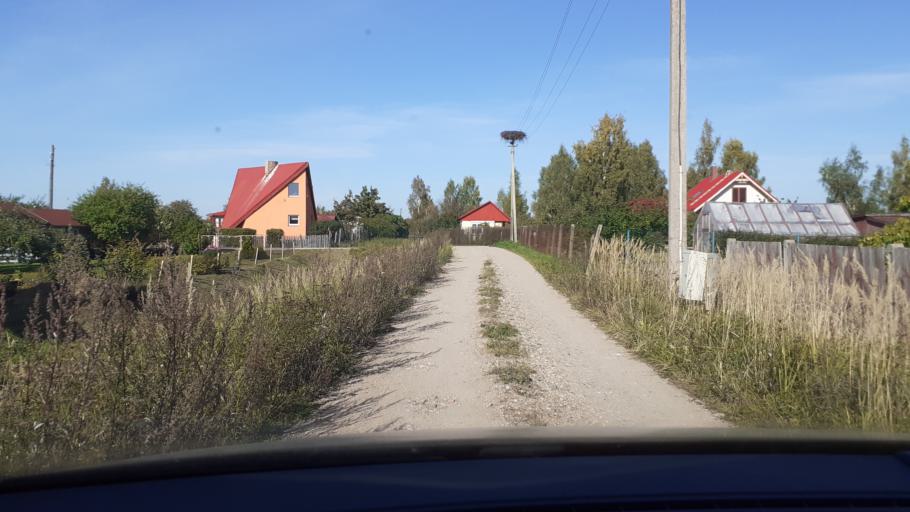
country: LV
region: Kuldigas Rajons
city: Kuldiga
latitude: 56.9499
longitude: 21.9779
